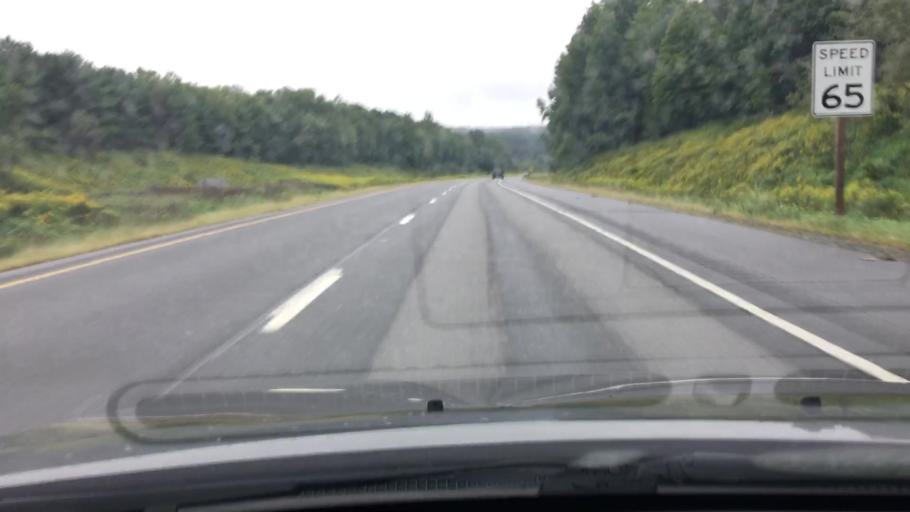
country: US
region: Pennsylvania
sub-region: Monroe County
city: Mountainhome
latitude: 41.3432
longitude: -75.3274
